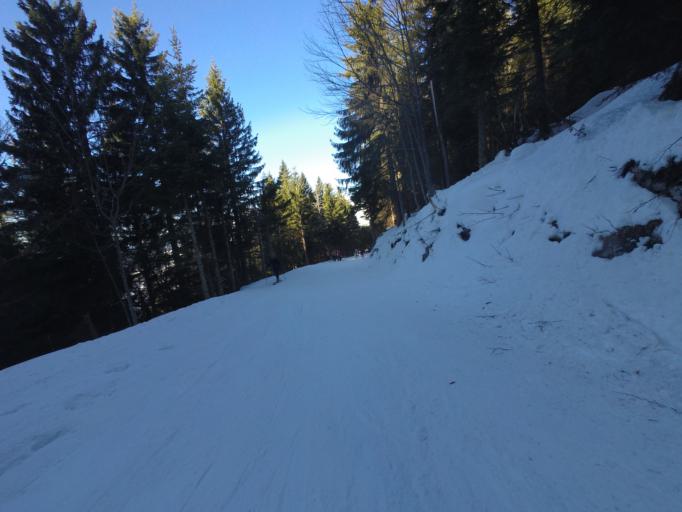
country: AT
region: Salzburg
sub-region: Politischer Bezirk Hallein
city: Scheffau am Tennengebirge
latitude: 47.6381
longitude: 13.2575
